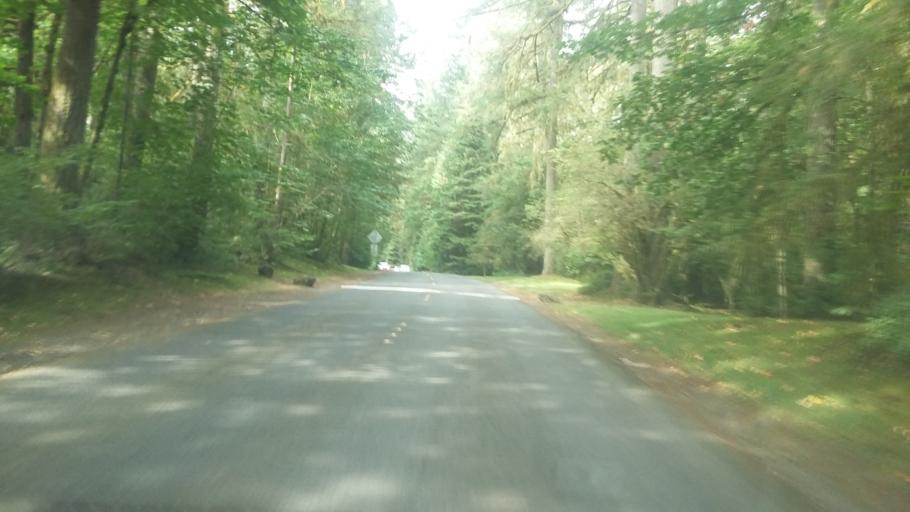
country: US
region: Washington
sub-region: Clark County
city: Lewisville
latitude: 45.8163
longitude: -122.5436
